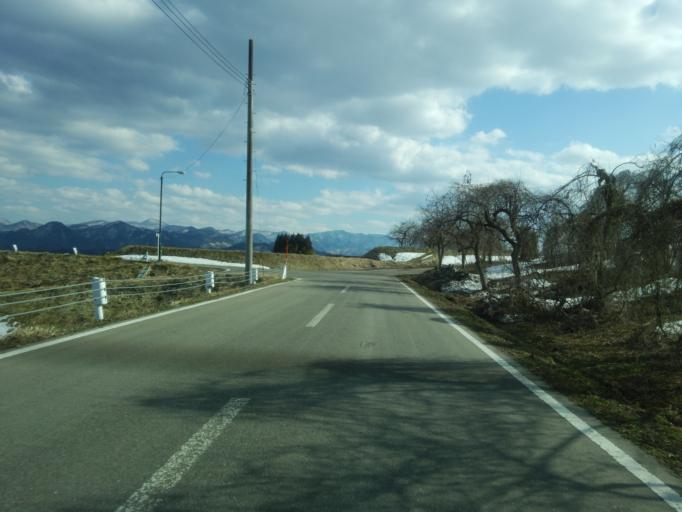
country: JP
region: Fukushima
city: Kitakata
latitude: 37.4522
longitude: 139.8035
